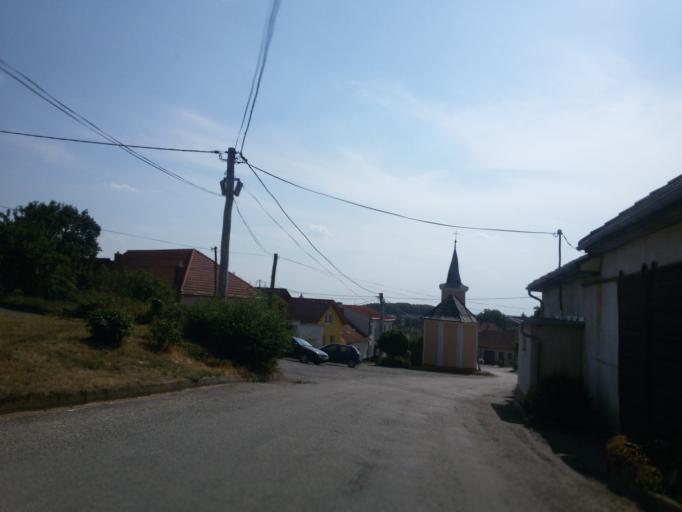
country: CZ
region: South Moravian
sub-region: Okres Brno-Venkov
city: Lomnice
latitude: 49.4444
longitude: 16.4593
